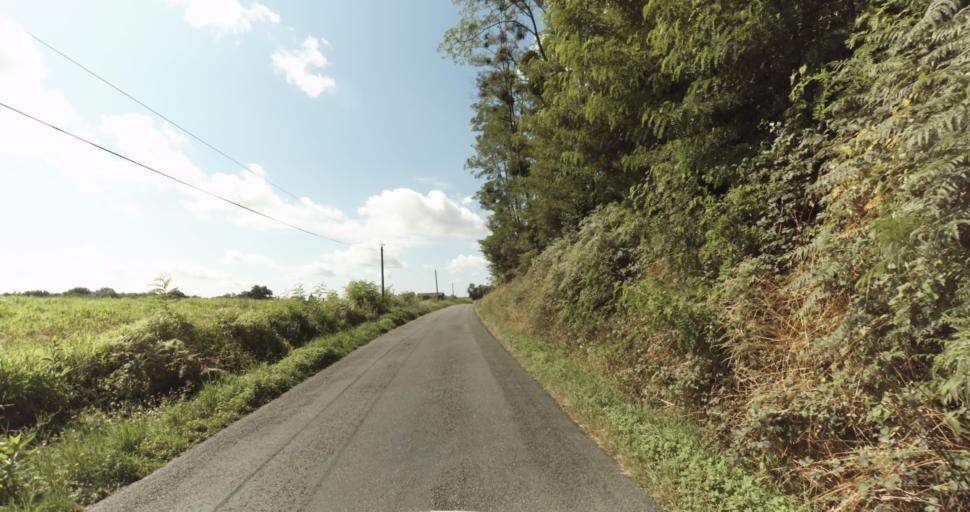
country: FR
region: Aquitaine
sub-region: Departement de la Gironde
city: Bazas
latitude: 44.4522
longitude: -0.2066
